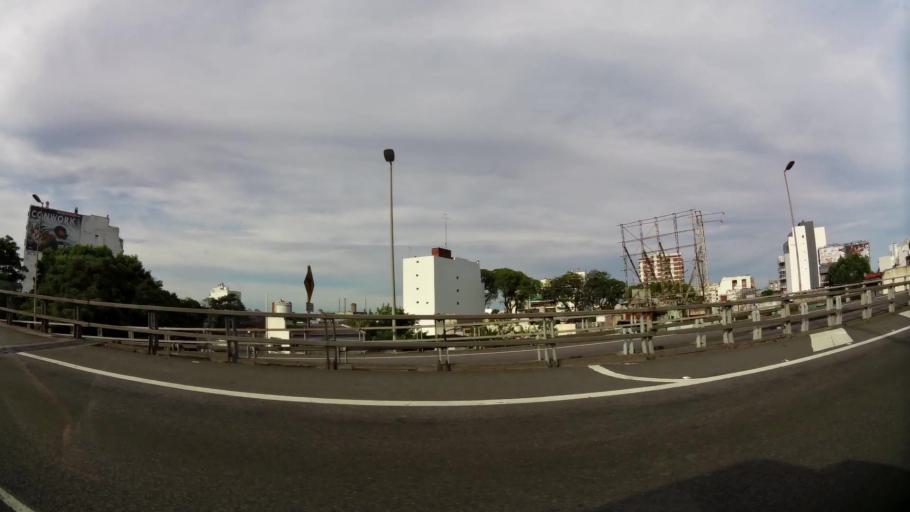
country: AR
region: Buenos Aires F.D.
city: Villa Santa Rita
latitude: -34.6368
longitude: -58.4954
